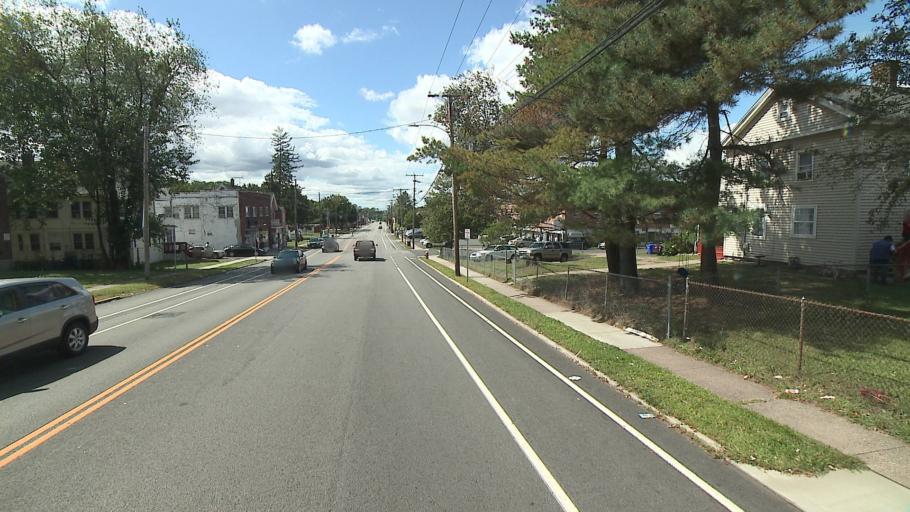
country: US
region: Connecticut
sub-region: Hartford County
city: East Hartford
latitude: 41.7797
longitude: -72.6077
